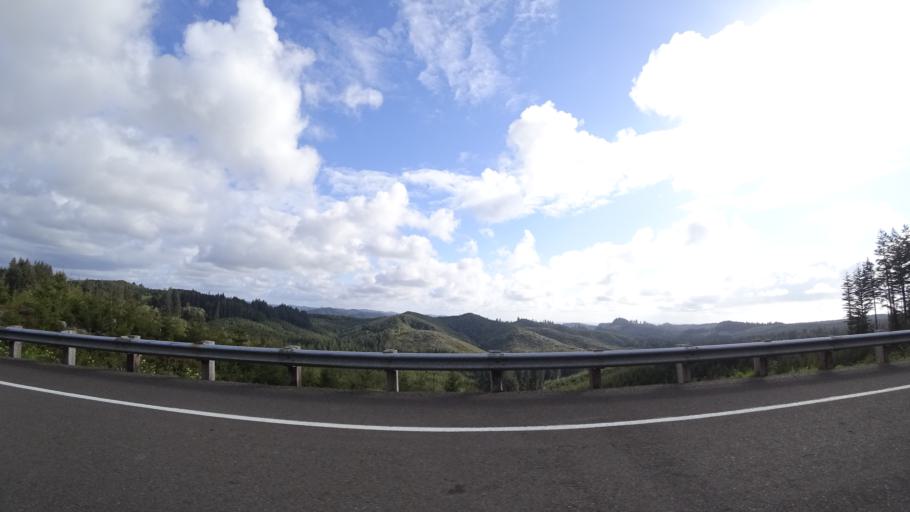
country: US
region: Oregon
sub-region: Douglas County
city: Reedsport
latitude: 43.7625
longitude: -124.1273
